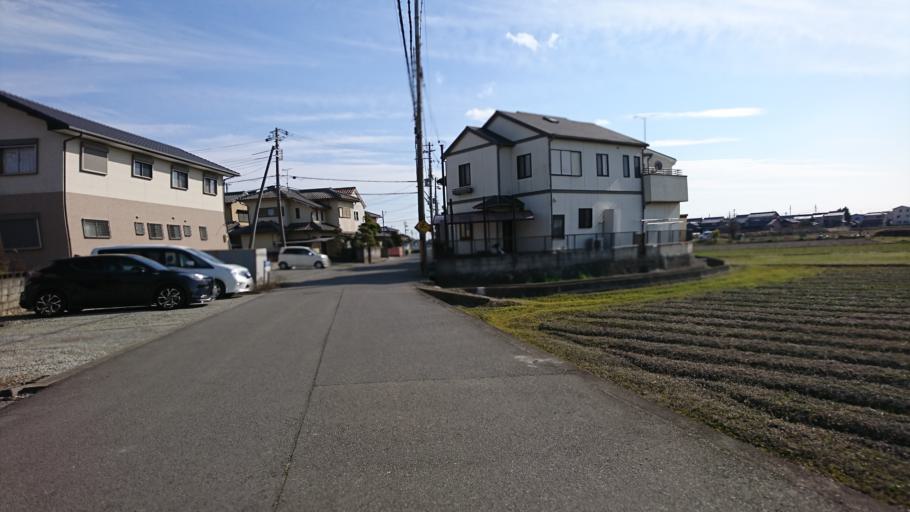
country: JP
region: Hyogo
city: Kakogawacho-honmachi
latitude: 34.7861
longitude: 134.8340
